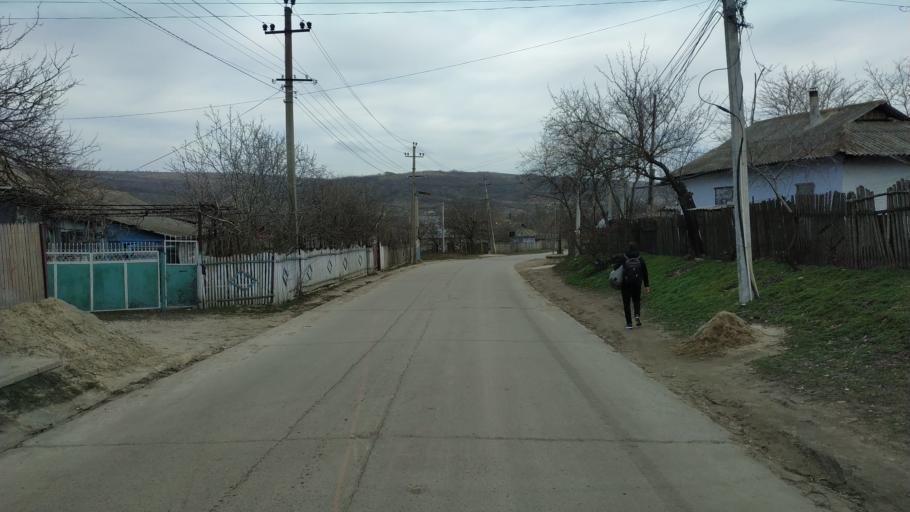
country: MD
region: Nisporeni
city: Nisporeni
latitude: 46.9263
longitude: 28.2627
